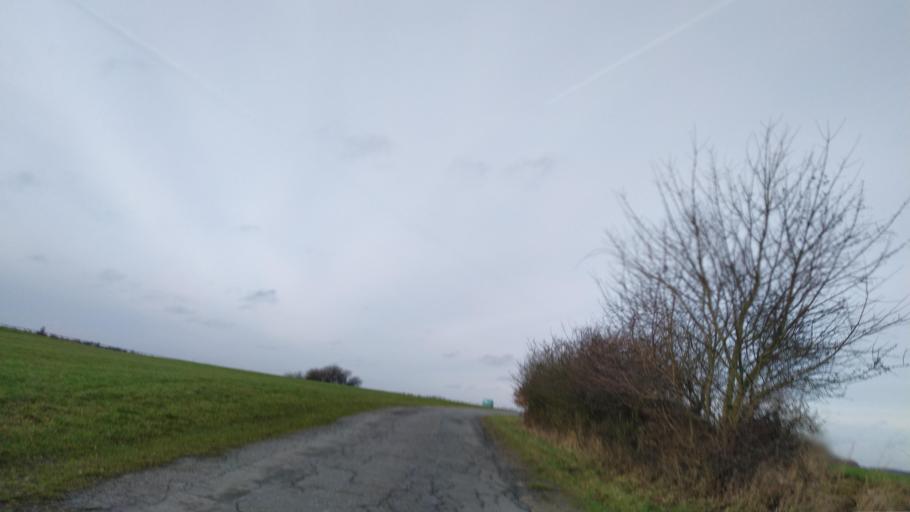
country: DE
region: Schleswig-Holstein
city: Neukirchen
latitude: 54.2016
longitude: 10.5961
